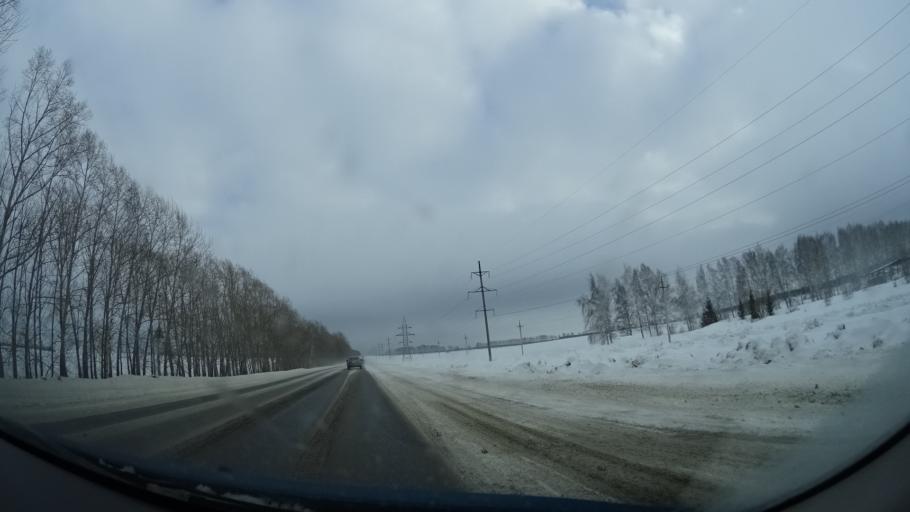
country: RU
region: Bashkortostan
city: Mikhaylovka
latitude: 54.8622
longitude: 55.7533
